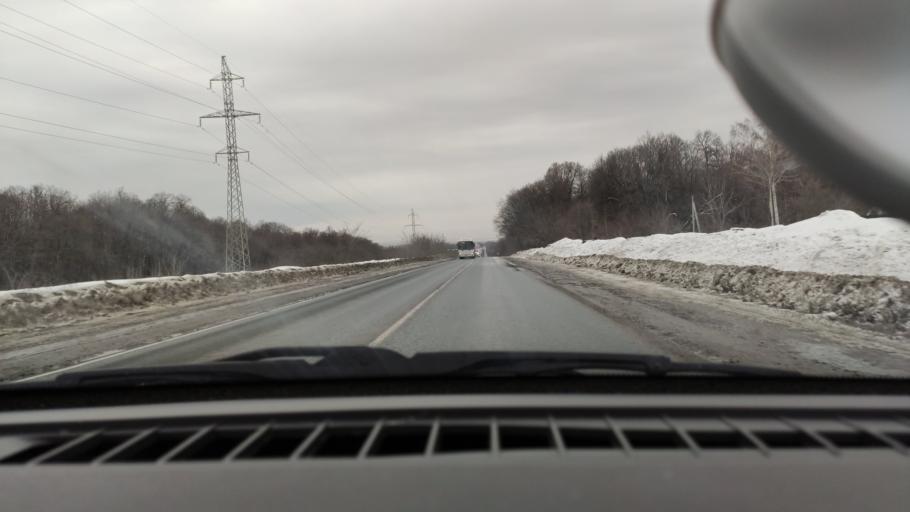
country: RU
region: Samara
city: Novosemeykino
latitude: 53.3311
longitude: 50.2568
